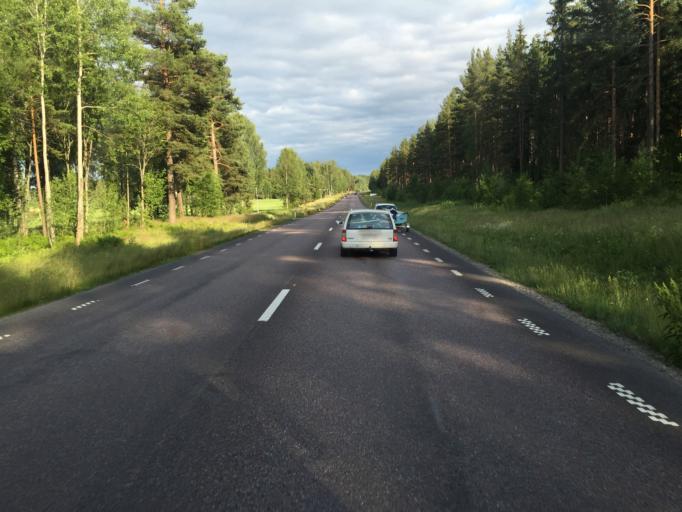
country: SE
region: Dalarna
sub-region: Borlange Kommun
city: Borlaenge
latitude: 60.5219
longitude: 15.3601
